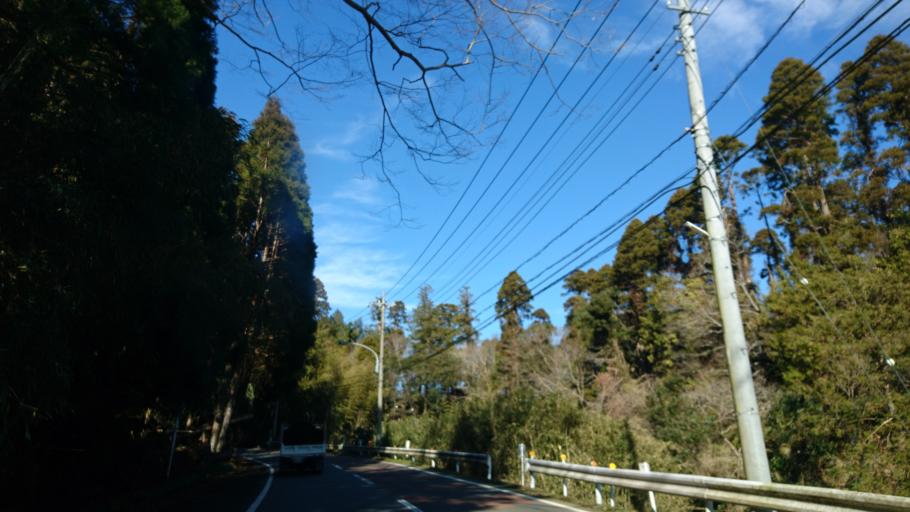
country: JP
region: Chiba
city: Yachimata
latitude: 35.6181
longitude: 140.3347
